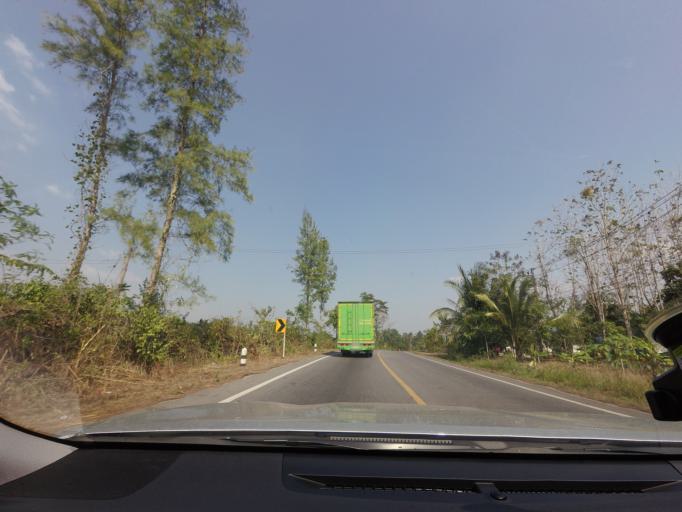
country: TH
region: Krabi
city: Plai Phraya
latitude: 8.5570
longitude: 98.8058
